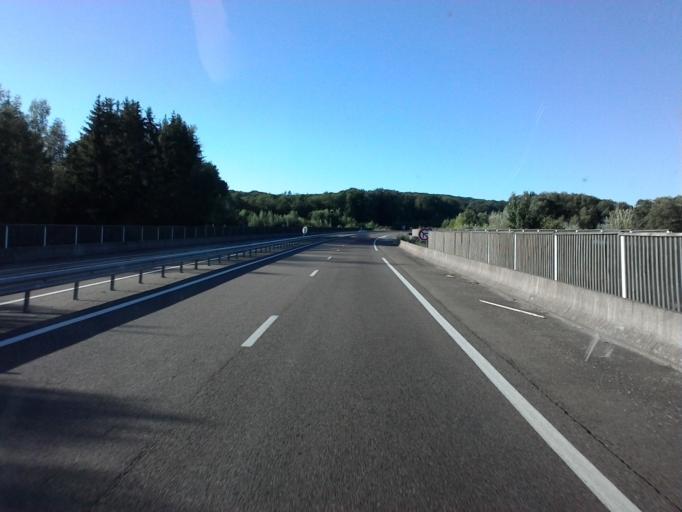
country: FR
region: Franche-Comte
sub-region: Departement de la Haute-Saone
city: Saint-Sauveur
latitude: 47.8188
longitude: 6.3942
